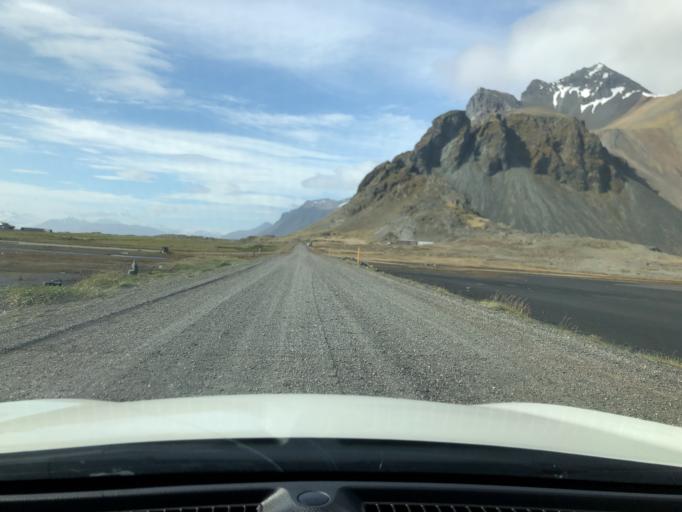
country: IS
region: East
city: Hoefn
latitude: 64.2517
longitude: -14.9883
